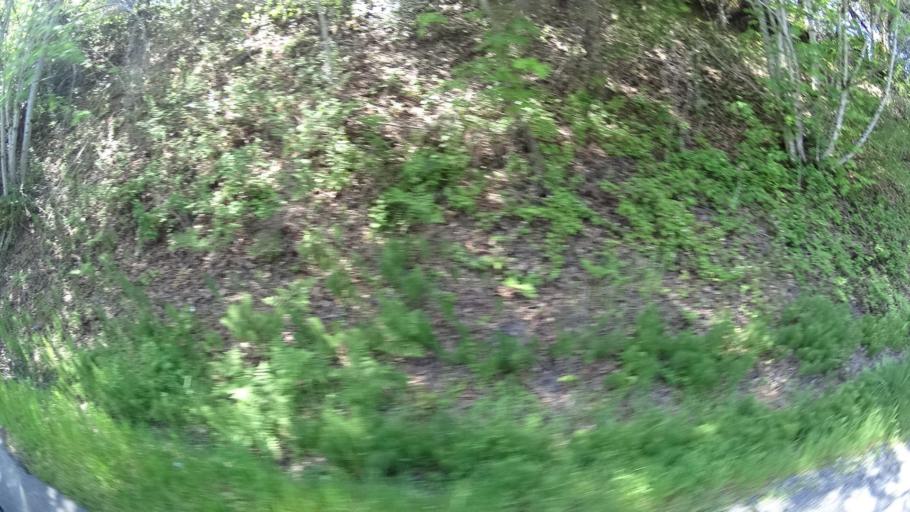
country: US
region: California
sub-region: Humboldt County
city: Redway
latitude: 40.1747
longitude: -123.6006
